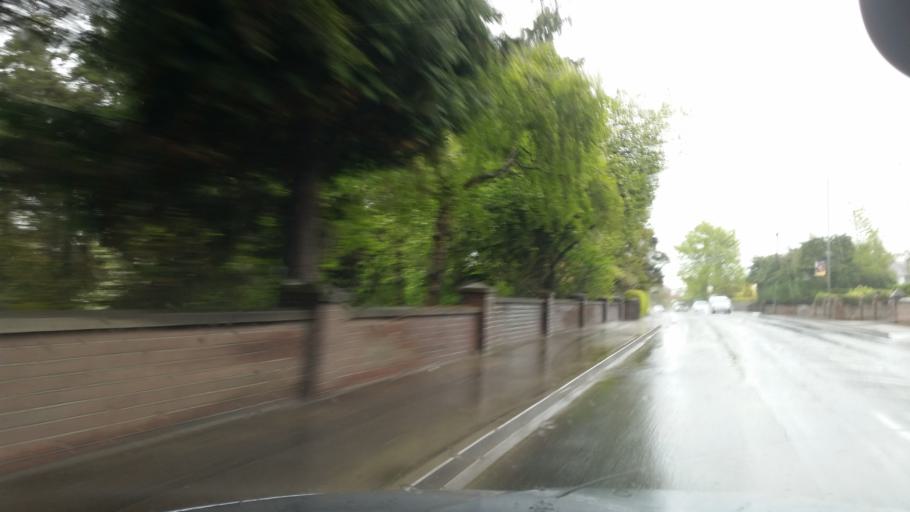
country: GB
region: Northern Ireland
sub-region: Strabane District
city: Strabane
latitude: 54.8388
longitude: -7.4553
